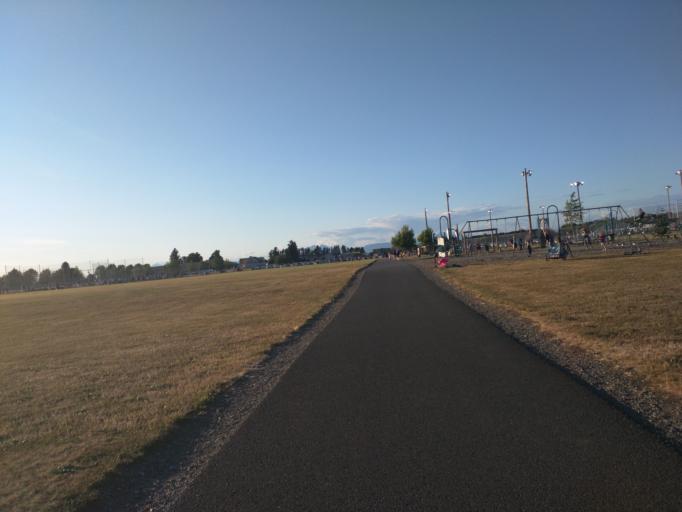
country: US
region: Washington
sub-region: Whatcom County
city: Lynden
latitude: 48.9572
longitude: -122.4382
